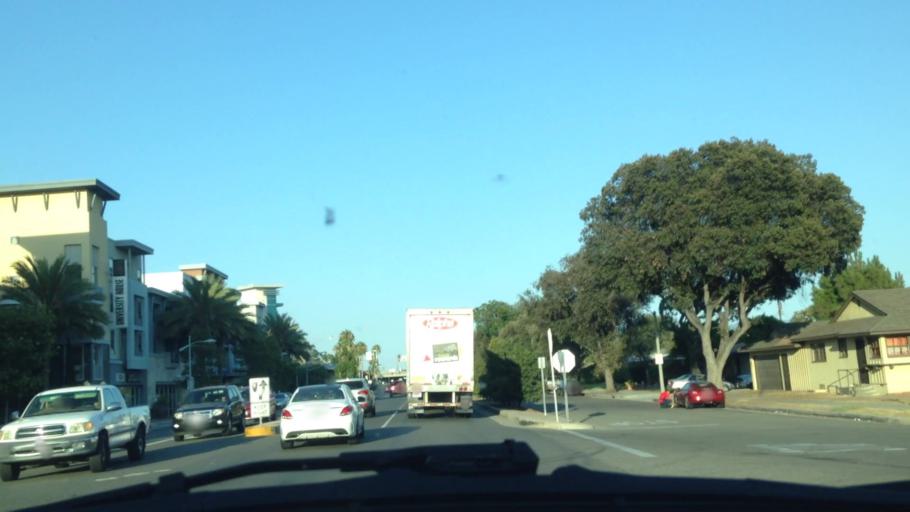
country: US
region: California
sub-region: Orange County
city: Placentia
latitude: 33.8742
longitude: -117.8863
